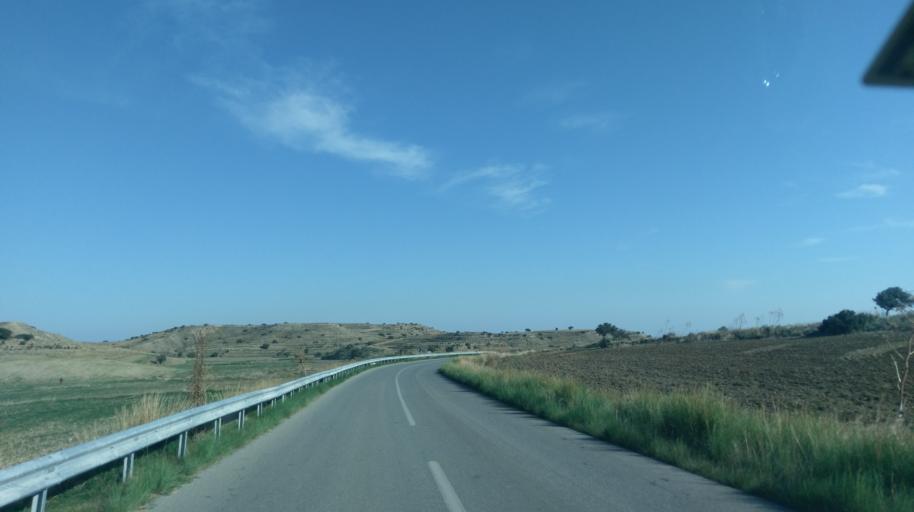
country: CY
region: Ammochostos
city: Trikomo
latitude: 35.3047
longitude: 33.8441
